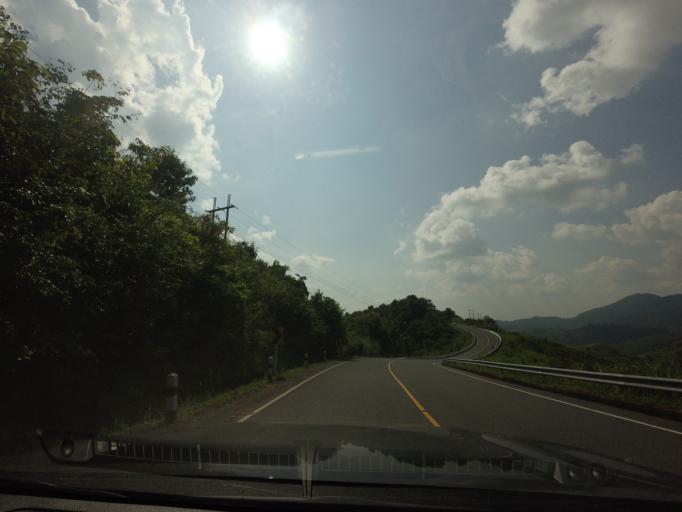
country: TH
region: Nan
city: Santi Suk
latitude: 18.9737
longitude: 101.0359
